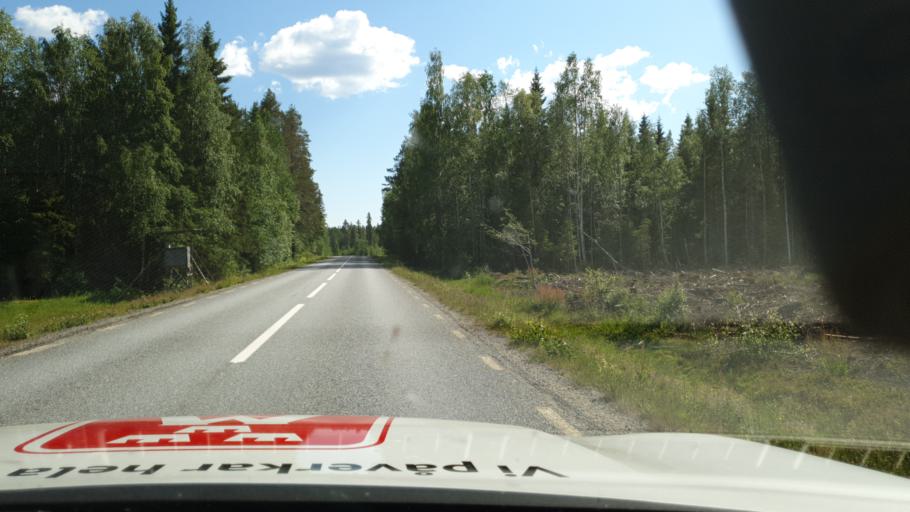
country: SE
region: Vaesterbotten
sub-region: Skelleftea Kommun
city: Burtraesk
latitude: 64.4428
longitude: 20.3957
